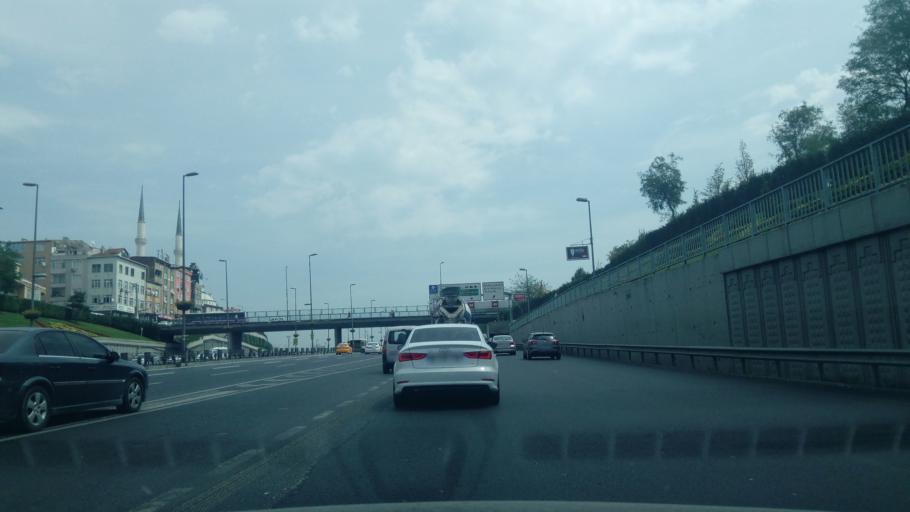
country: TR
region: Istanbul
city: Sisli
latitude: 41.0547
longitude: 28.9564
